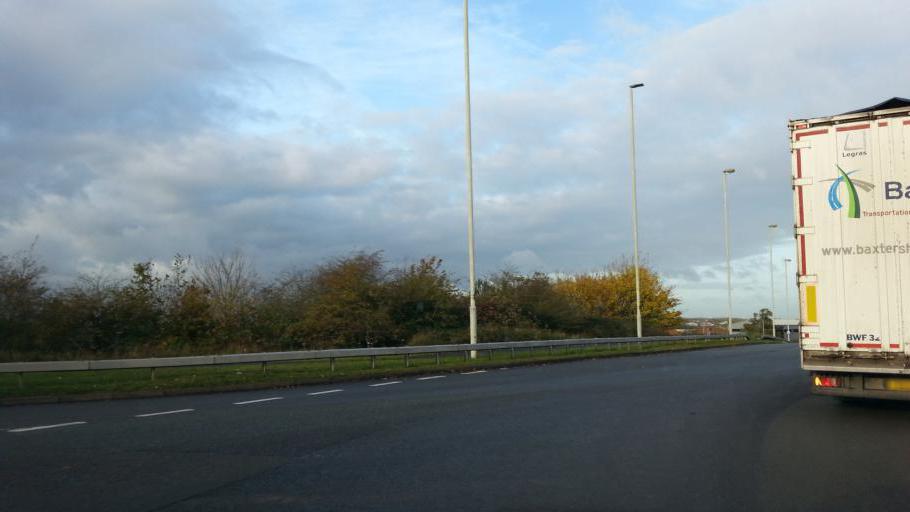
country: GB
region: England
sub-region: Leicestershire
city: Coalville
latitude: 52.7084
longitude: -1.3411
